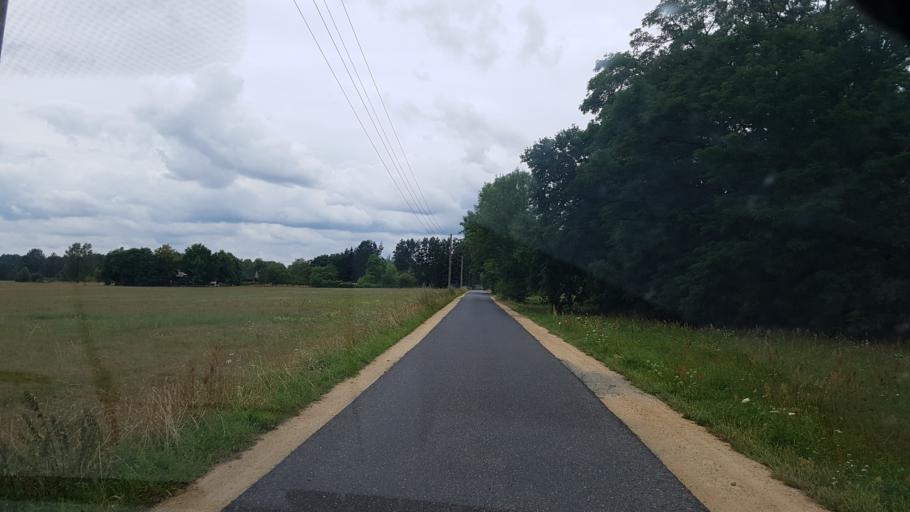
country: DE
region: Saxony
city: Rietschen
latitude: 51.3845
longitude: 14.7828
